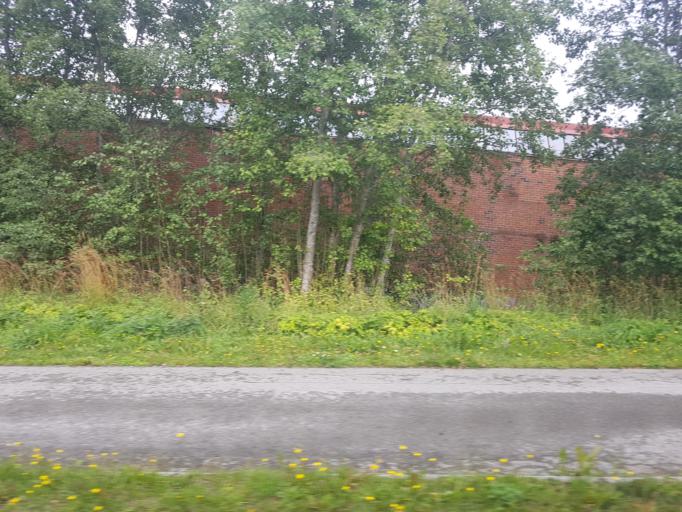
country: NO
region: Sor-Trondelag
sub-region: Trondheim
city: Trondheim
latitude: 63.3871
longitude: 10.3994
